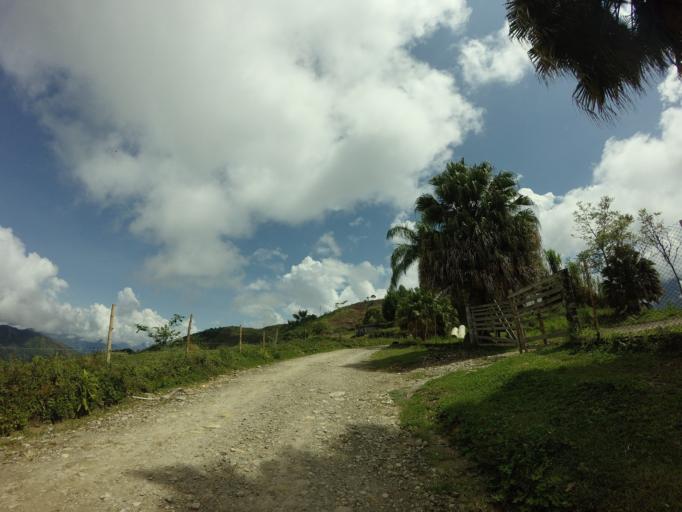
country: CO
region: Antioquia
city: Narino
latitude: 5.5038
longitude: -75.1803
